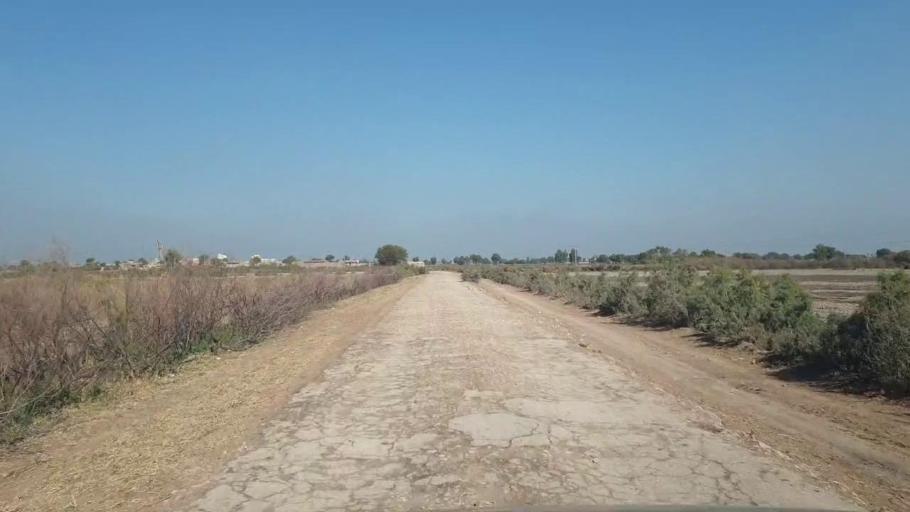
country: PK
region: Sindh
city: Bhit Shah
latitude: 25.8797
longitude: 68.5268
